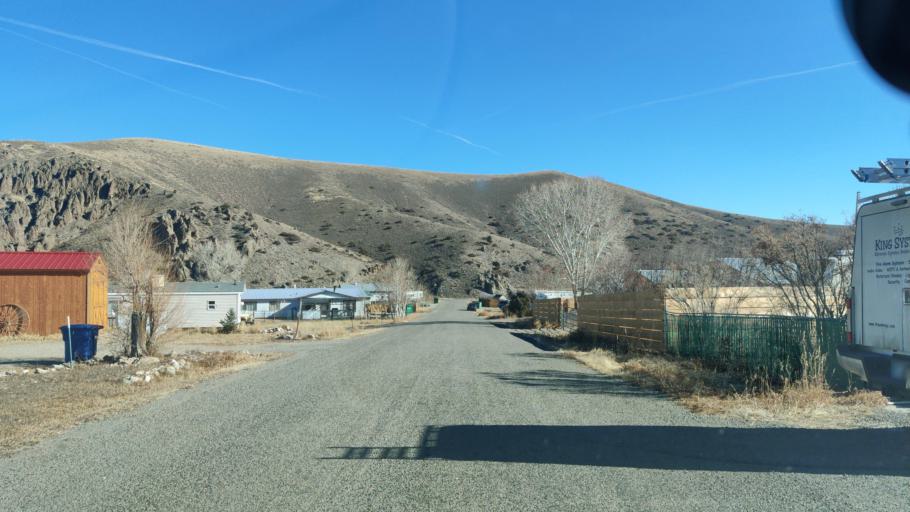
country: US
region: Colorado
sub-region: Gunnison County
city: Gunnison
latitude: 38.5766
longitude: -106.9660
